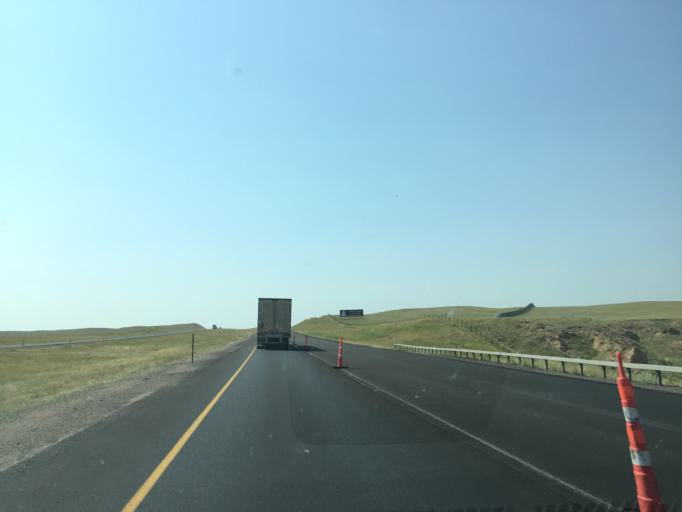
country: US
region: Wyoming
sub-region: Laramie County
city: Ranchettes
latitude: 41.3236
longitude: -104.8618
